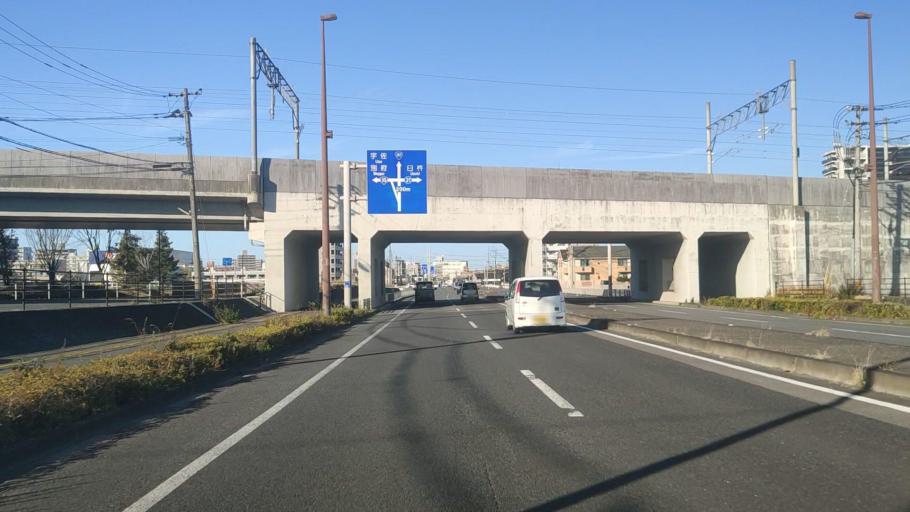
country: JP
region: Oita
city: Oita
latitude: 33.2286
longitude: 131.6188
